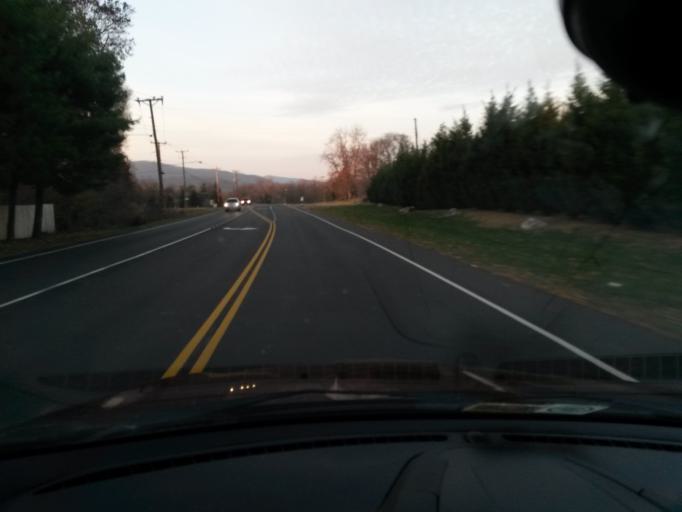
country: US
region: Virginia
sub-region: Roanoke County
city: Hollins
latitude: 37.3387
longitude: -79.9420
